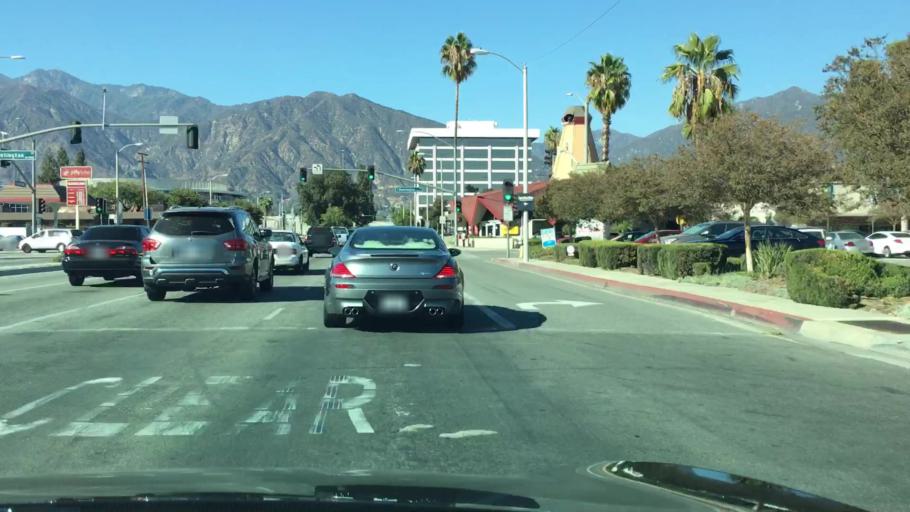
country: US
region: California
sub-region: Los Angeles County
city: Arcadia
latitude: 34.1395
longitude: -118.0314
